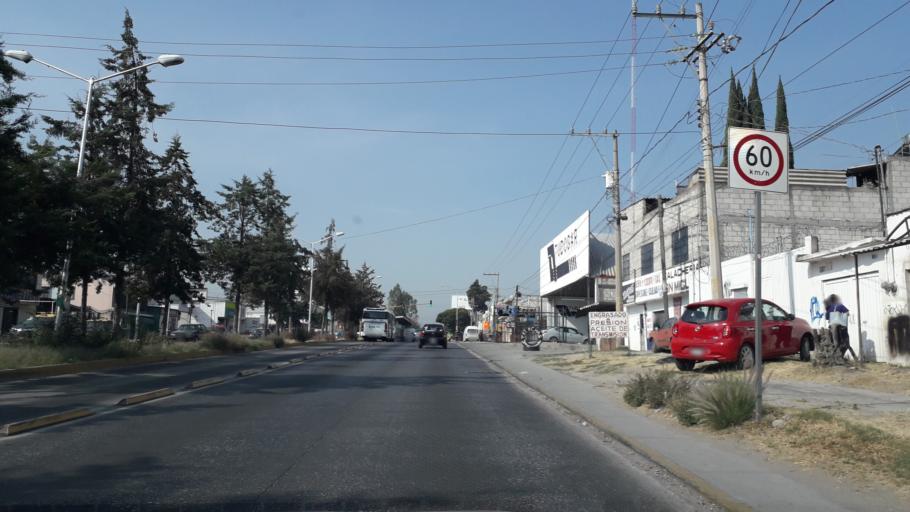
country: MX
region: Puebla
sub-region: Puebla
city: El Capulo (La Quebradora)
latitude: 18.9855
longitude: -98.2501
